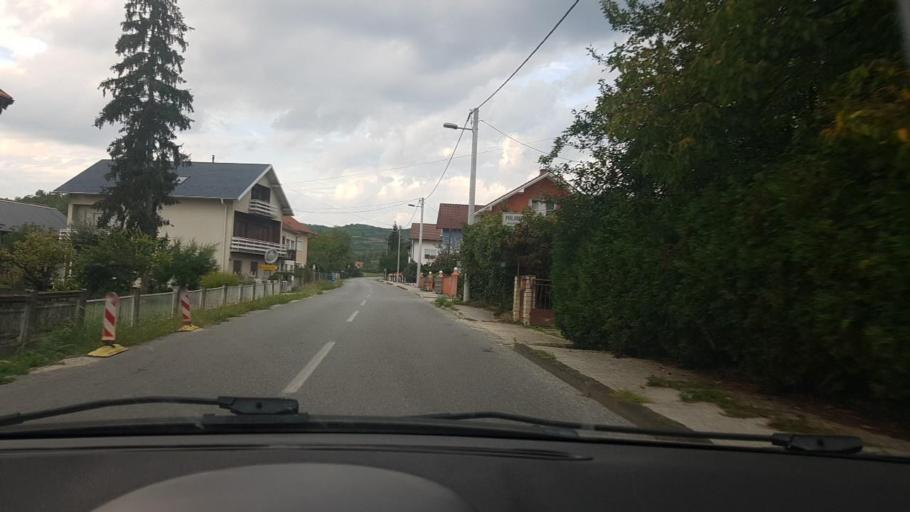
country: HR
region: Krapinsko-Zagorska
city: Marija Bistrica
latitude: 45.9222
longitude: 16.1708
